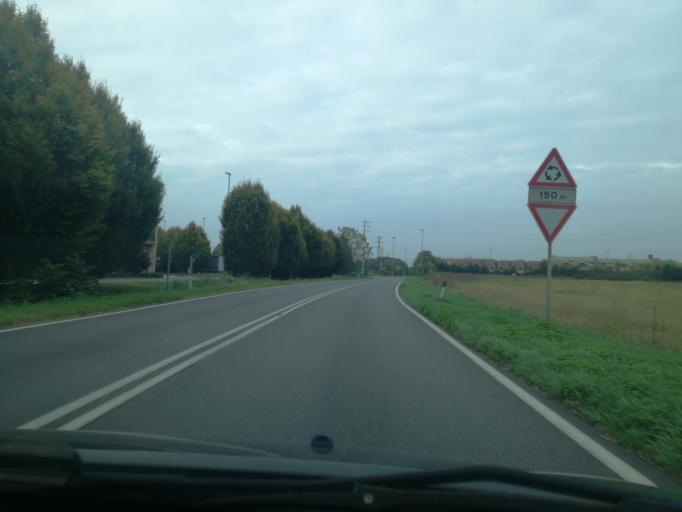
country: IT
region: Lombardy
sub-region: Provincia di Monza e Brianza
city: Bellusco
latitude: 45.6272
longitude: 9.4152
